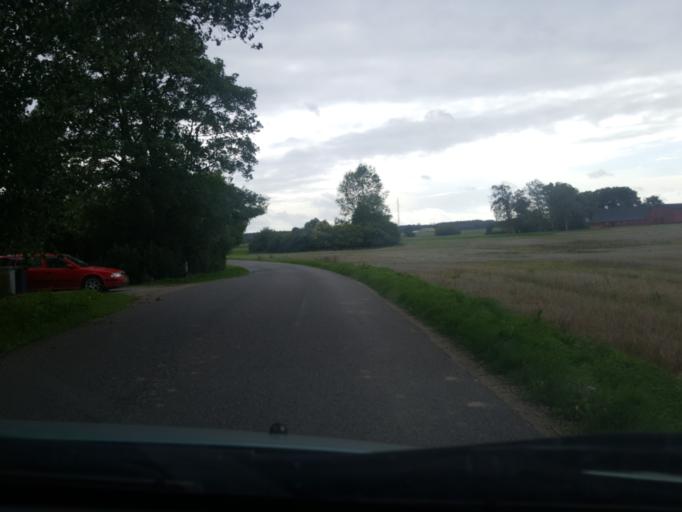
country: DK
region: Zealand
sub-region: Soro Kommune
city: Soro
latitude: 55.4678
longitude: 11.5186
